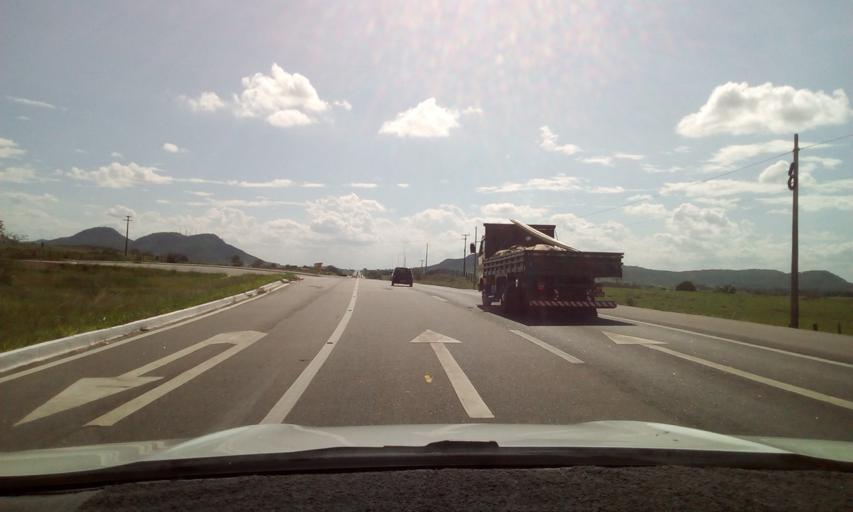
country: BR
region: Paraiba
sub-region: Gurinhem
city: Gurinhem
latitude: -7.1663
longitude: -35.3603
